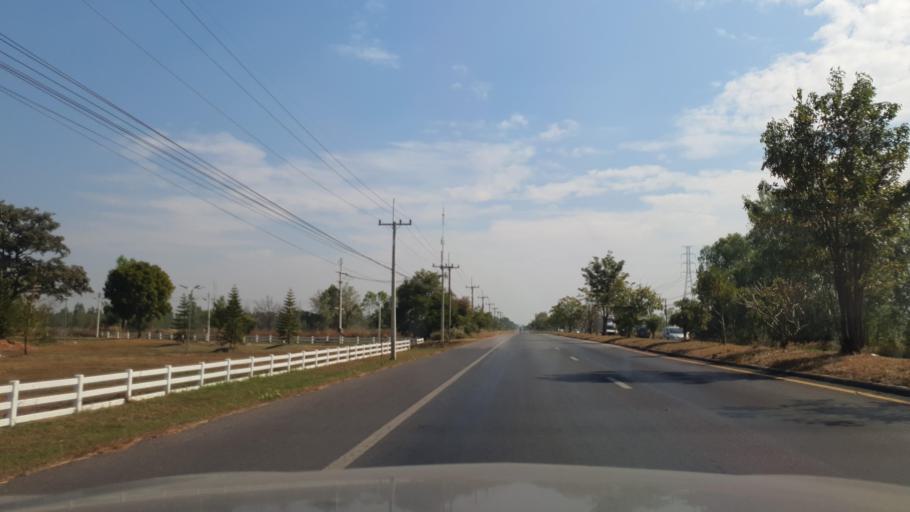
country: TH
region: Maha Sarakham
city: Kantharawichai
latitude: 16.3921
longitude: 103.2845
